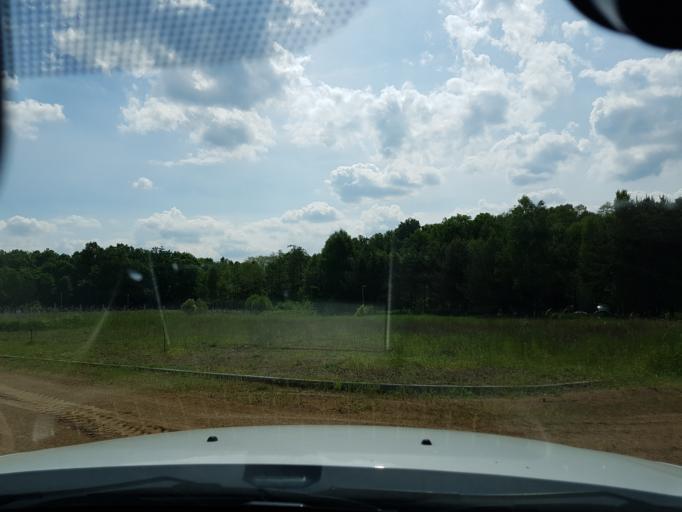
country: PL
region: West Pomeranian Voivodeship
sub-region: Powiat stargardzki
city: Insko
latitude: 53.4796
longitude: 15.6029
